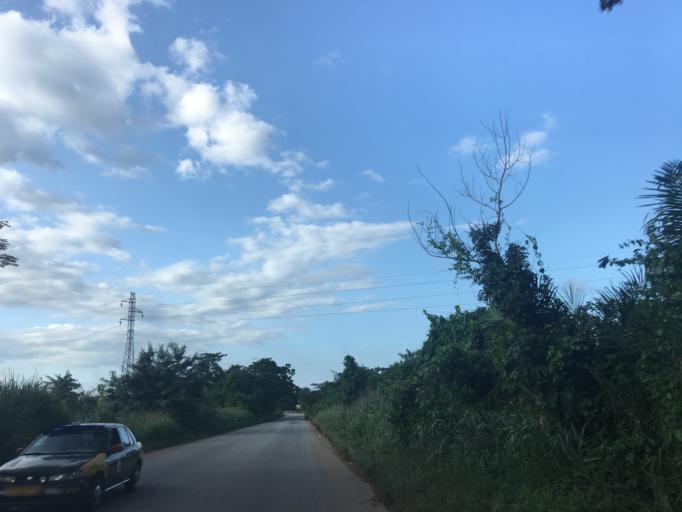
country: GH
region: Western
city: Bibiani
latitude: 6.3253
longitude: -2.2513
